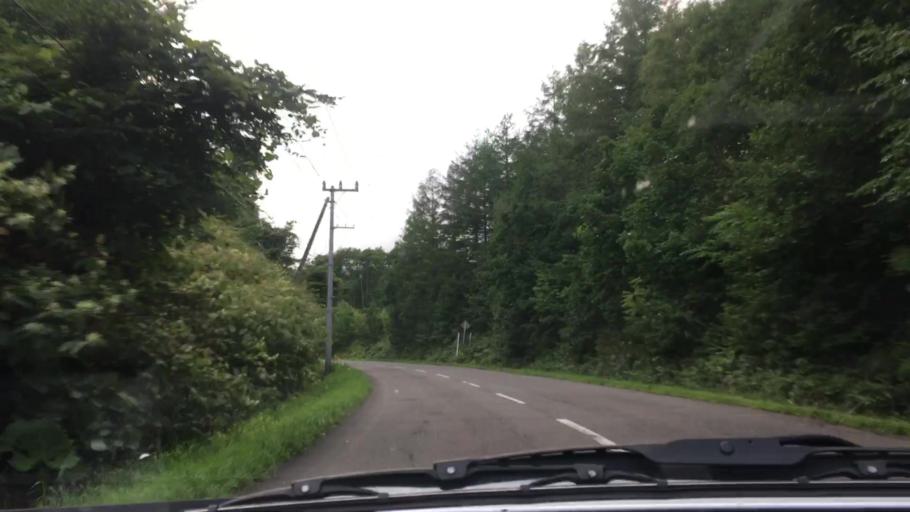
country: JP
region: Hokkaido
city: Otofuke
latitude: 43.1473
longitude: 142.8718
